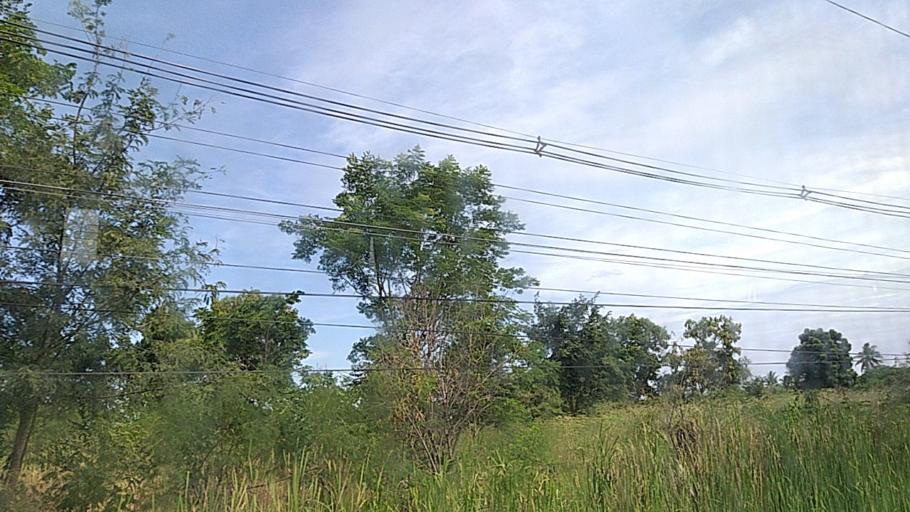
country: TH
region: Maha Sarakham
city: Chiang Yuen
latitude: 16.4426
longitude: 102.9860
